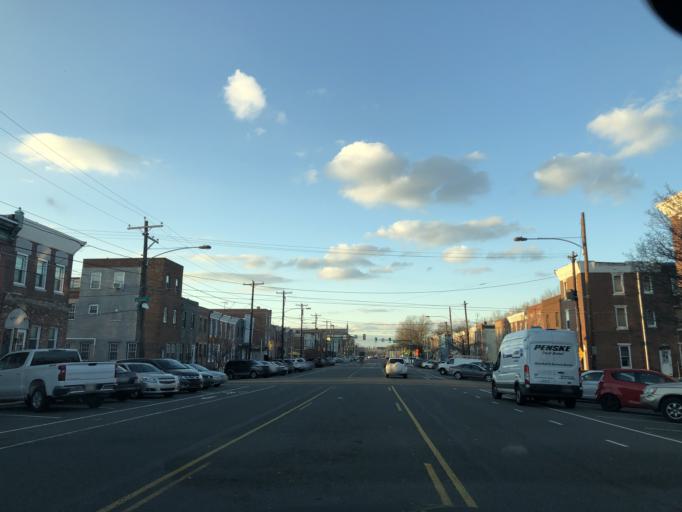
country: US
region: New Jersey
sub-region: Camden County
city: Camden
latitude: 39.9789
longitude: -75.1154
